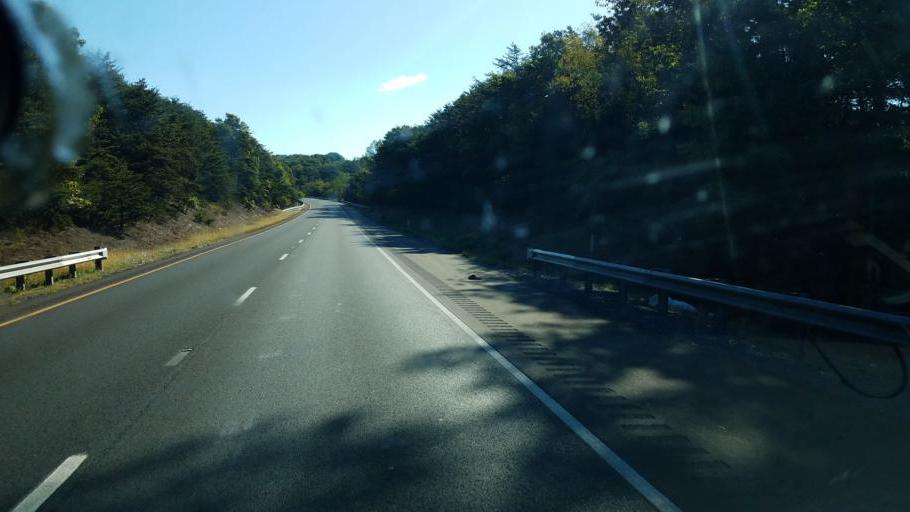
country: US
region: Maryland
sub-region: Washington County
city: Wilson-Conococheague
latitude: 39.6273
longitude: -77.9765
